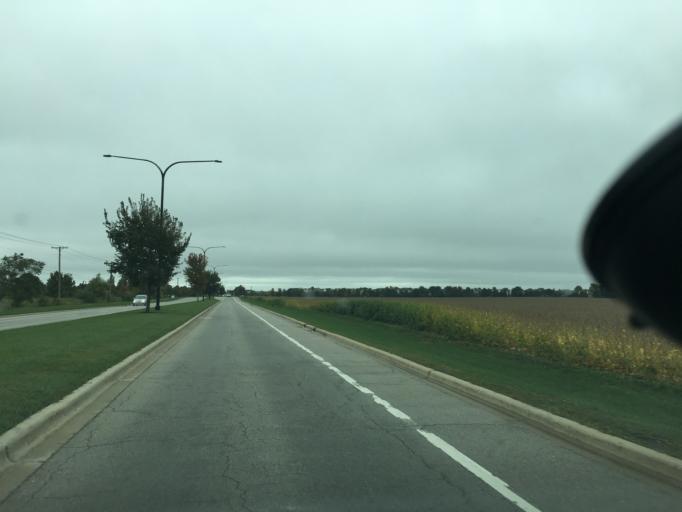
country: US
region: Illinois
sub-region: Will County
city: Plainfield
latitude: 41.6513
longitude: -88.2212
